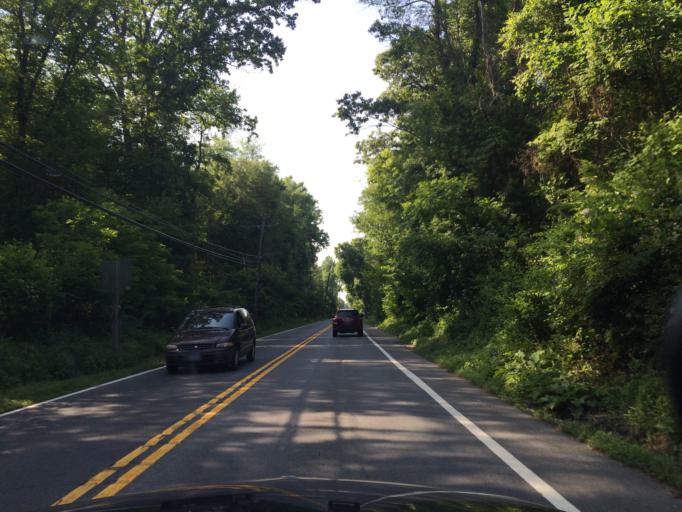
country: US
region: Maryland
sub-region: Montgomery County
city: Olney
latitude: 39.1826
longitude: -77.0623
